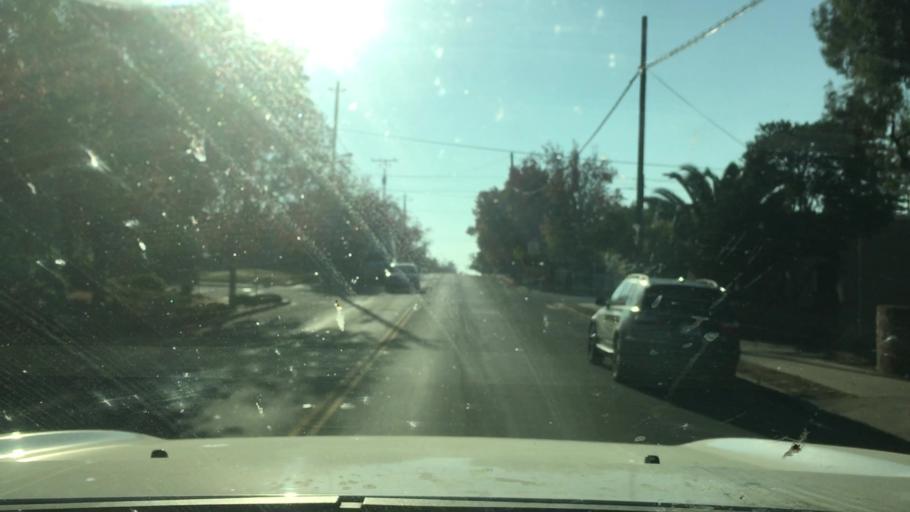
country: US
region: California
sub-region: San Luis Obispo County
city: San Luis Obispo
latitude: 35.2738
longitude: -120.6600
